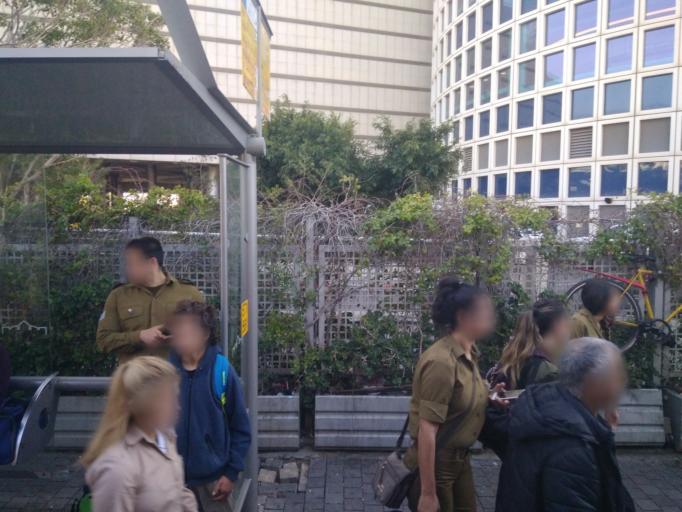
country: IL
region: Tel Aviv
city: Tel Aviv
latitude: 32.0746
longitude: 34.7916
